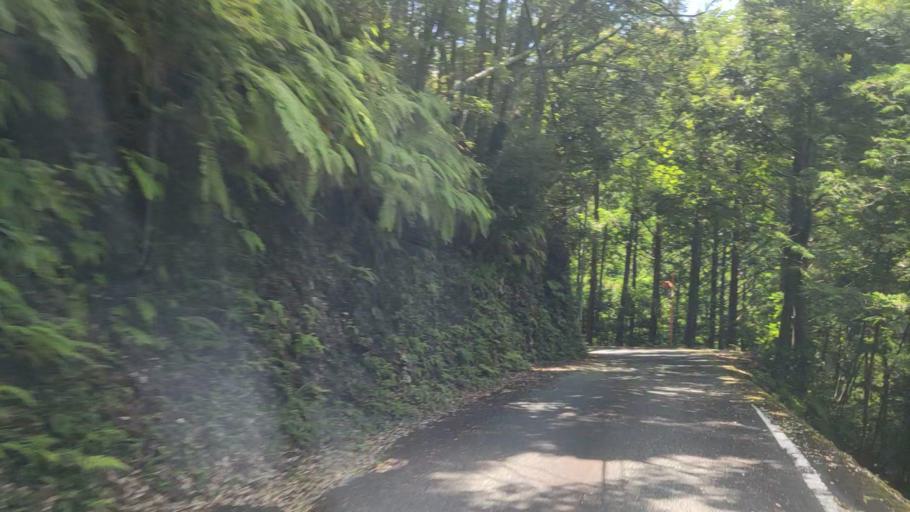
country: JP
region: Wakayama
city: Shingu
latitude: 33.9062
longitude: 135.8681
